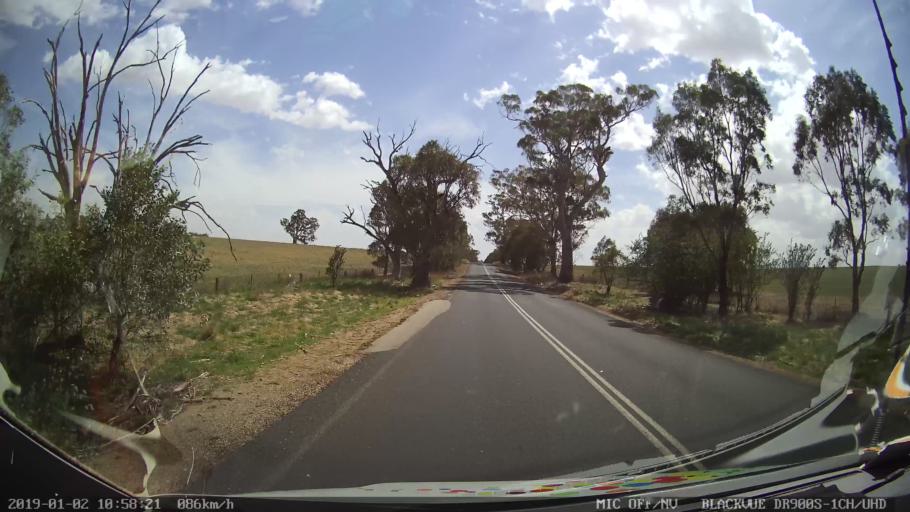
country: AU
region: New South Wales
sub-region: Cootamundra
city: Cootamundra
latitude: -34.6254
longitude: 148.2905
